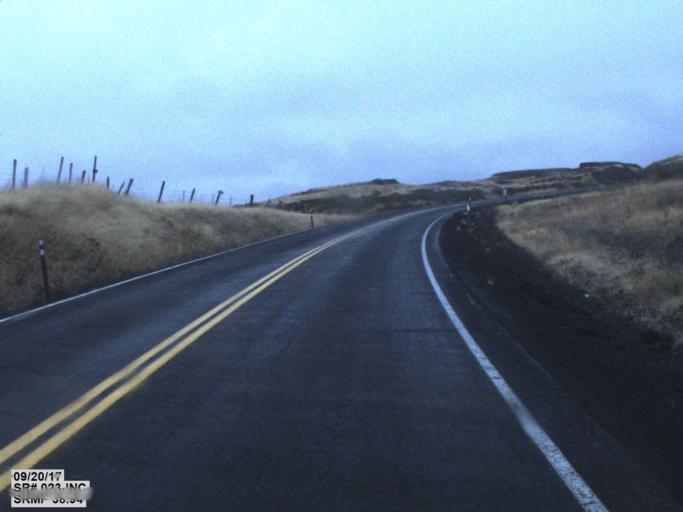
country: US
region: Washington
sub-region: Spokane County
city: Medical Lake
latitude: 47.2541
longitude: -117.9307
